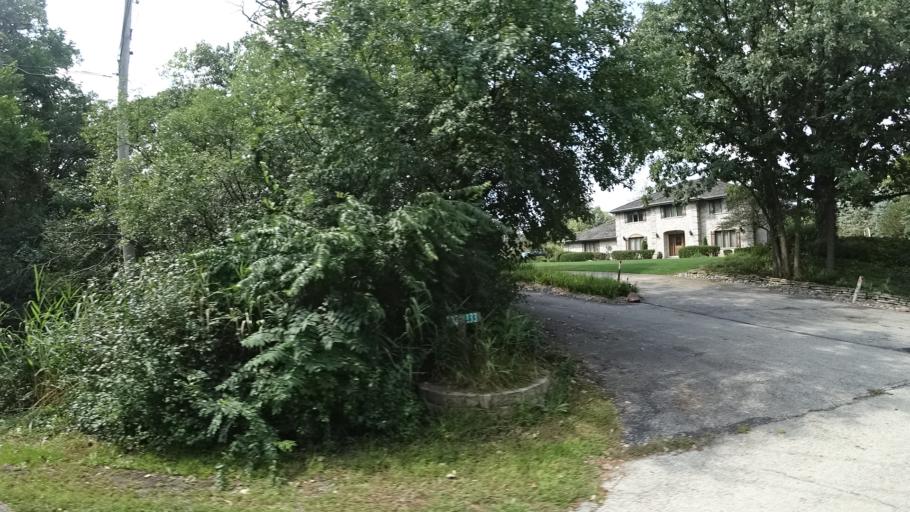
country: US
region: Illinois
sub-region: Will County
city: Goodings Grove
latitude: 41.6590
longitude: -87.8953
